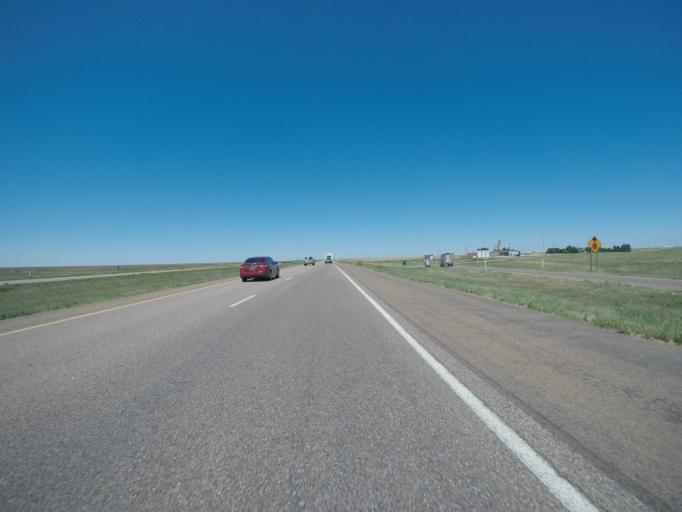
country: US
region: Kansas
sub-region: Trego County
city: WaKeeney
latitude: 38.9845
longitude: -99.7404
